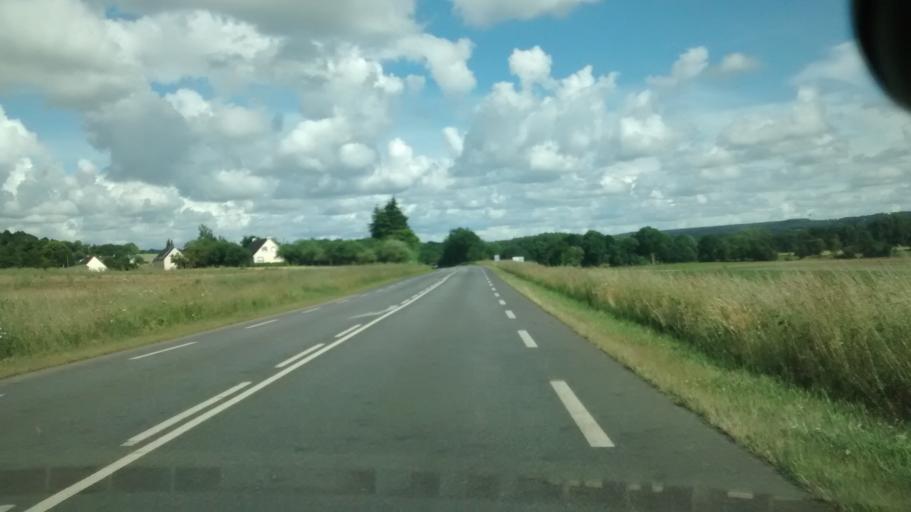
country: FR
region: Brittany
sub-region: Departement du Morbihan
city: Malestroit
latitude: 47.8391
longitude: -2.4058
